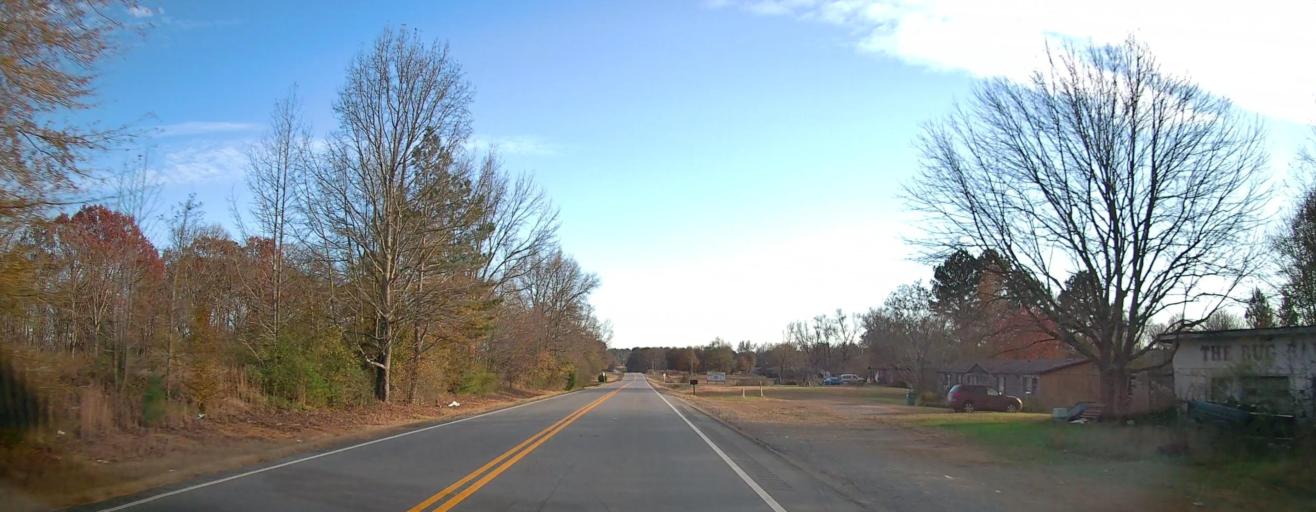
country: US
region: Alabama
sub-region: Marshall County
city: Arab
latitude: 34.2995
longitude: -86.5933
